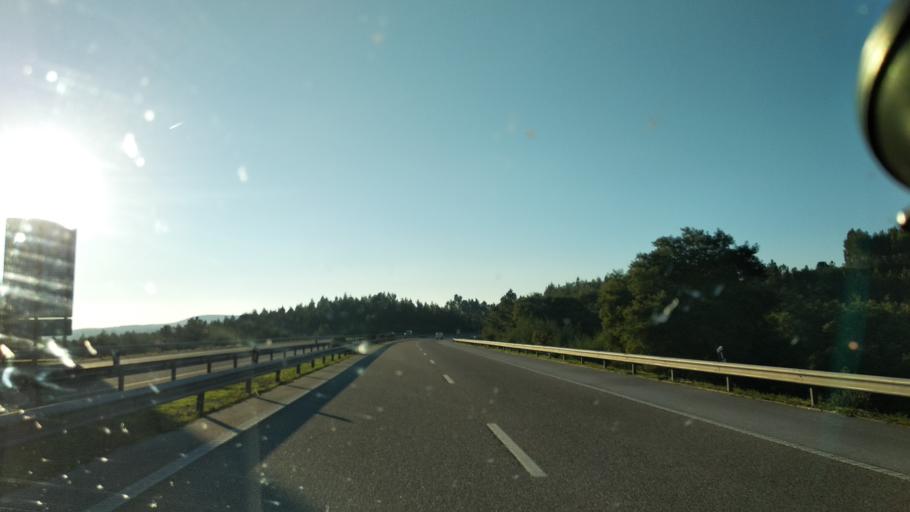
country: PT
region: Santarem
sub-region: Constancia
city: Constancia
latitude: 39.4849
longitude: -8.3683
